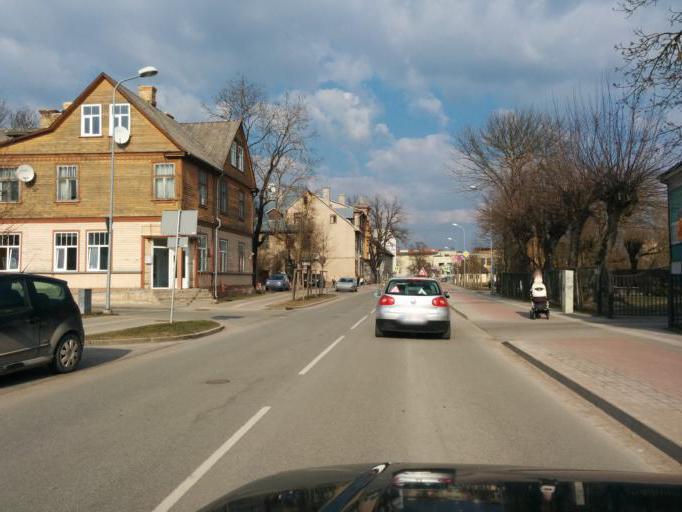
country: LV
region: Jelgava
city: Jelgava
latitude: 56.6456
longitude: 23.7126
